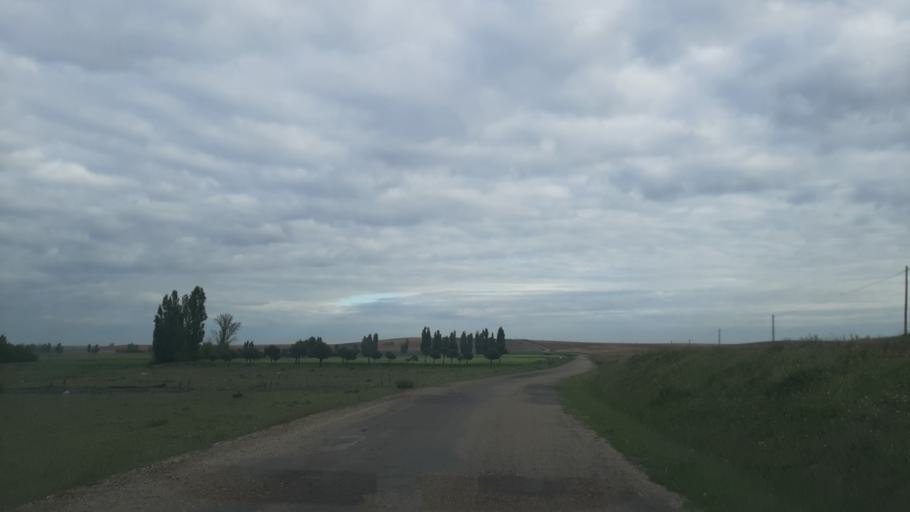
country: ES
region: Castille and Leon
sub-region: Provincia de Salamanca
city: Palaciosrubios
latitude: 41.0587
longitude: -5.1984
